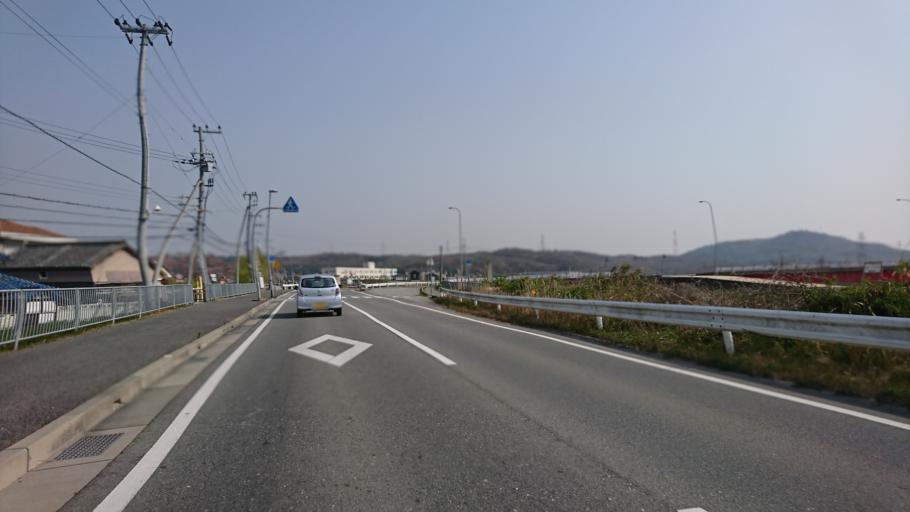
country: JP
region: Hyogo
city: Ono
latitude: 34.8238
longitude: 134.9360
